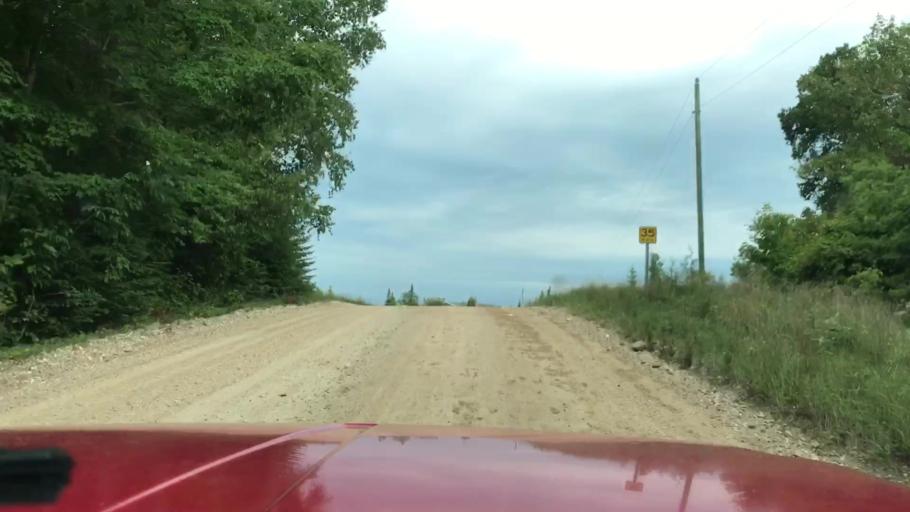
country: US
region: Michigan
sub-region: Charlevoix County
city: Charlevoix
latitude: 45.7369
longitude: -85.5589
